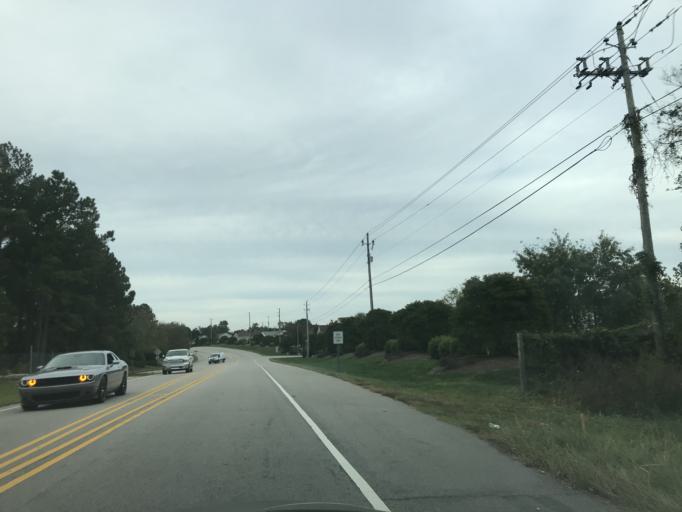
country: US
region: North Carolina
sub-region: Wake County
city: Rolesville
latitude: 35.8767
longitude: -78.5104
